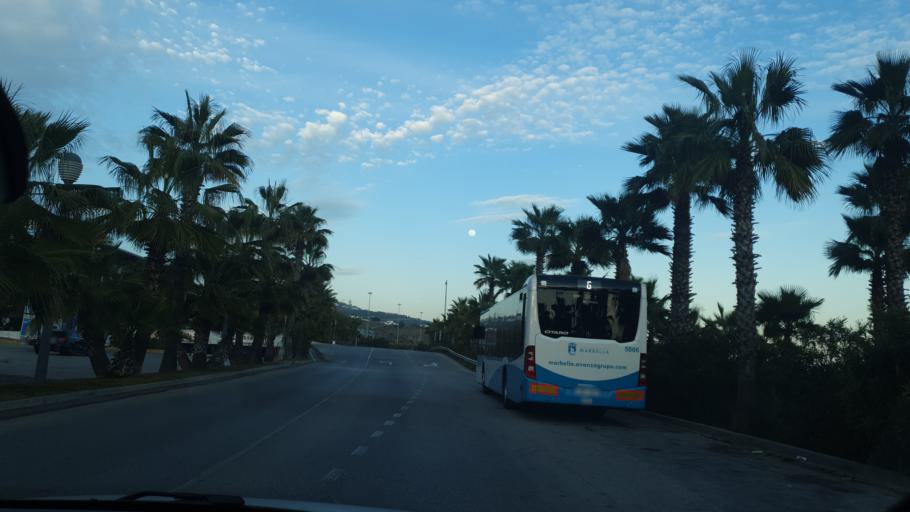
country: ES
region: Andalusia
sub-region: Provincia de Malaga
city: Marbella
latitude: 36.5205
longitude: -4.8738
